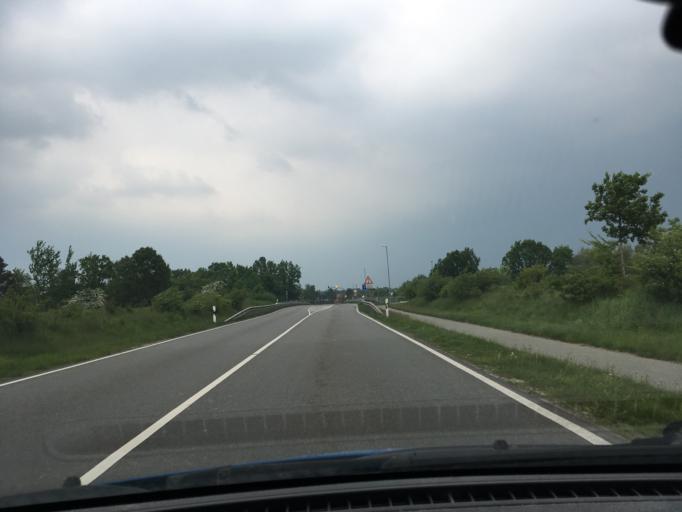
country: DE
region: Lower Saxony
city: Seevetal
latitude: 53.3794
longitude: 9.9868
